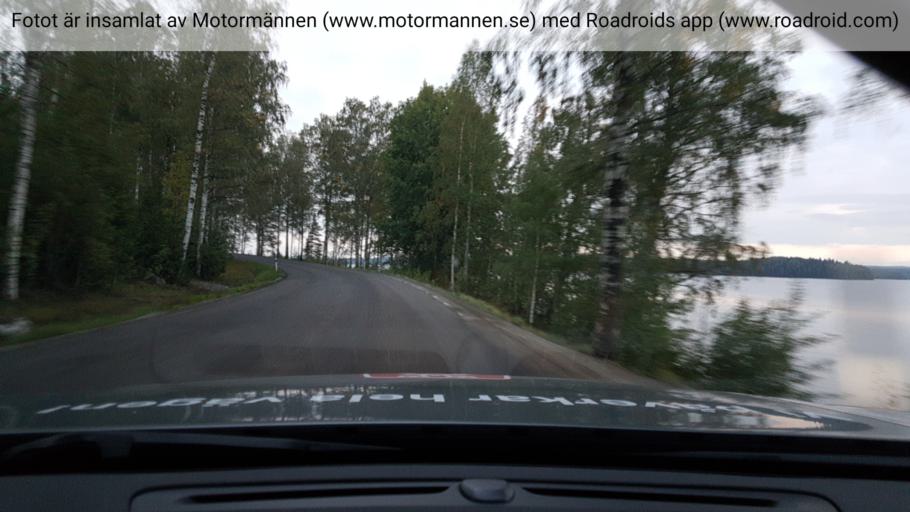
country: SE
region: OErebro
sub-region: Nora Kommun
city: As
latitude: 59.4971
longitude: 14.9504
